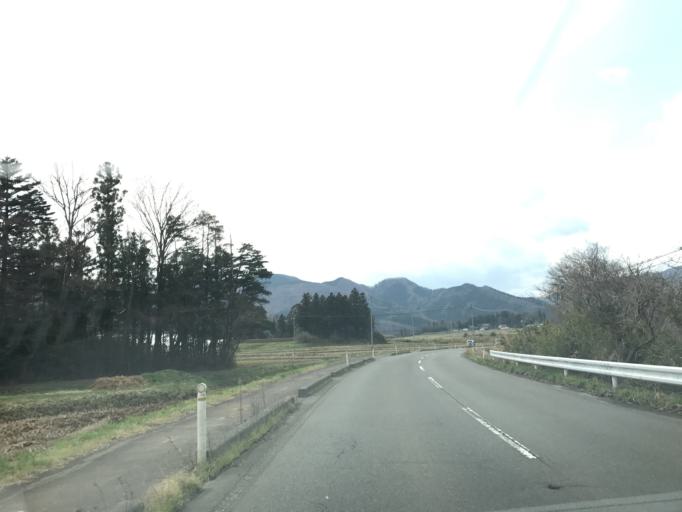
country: JP
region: Miyagi
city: Shiroishi
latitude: 38.0128
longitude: 140.5970
